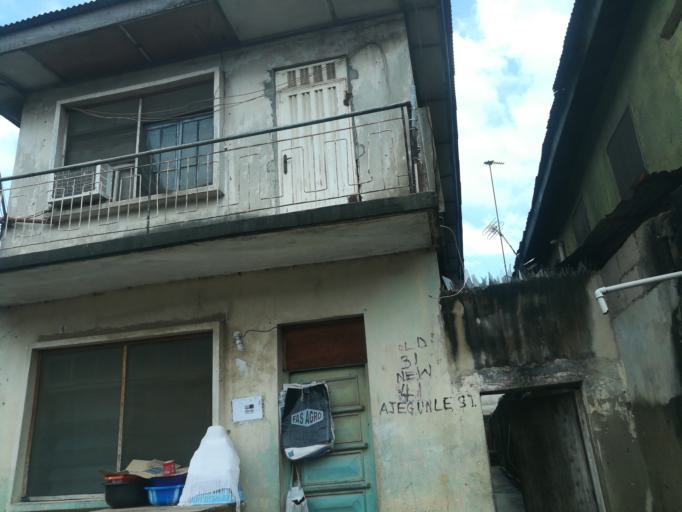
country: NG
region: Lagos
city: Somolu
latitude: 6.5354
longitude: 3.3634
